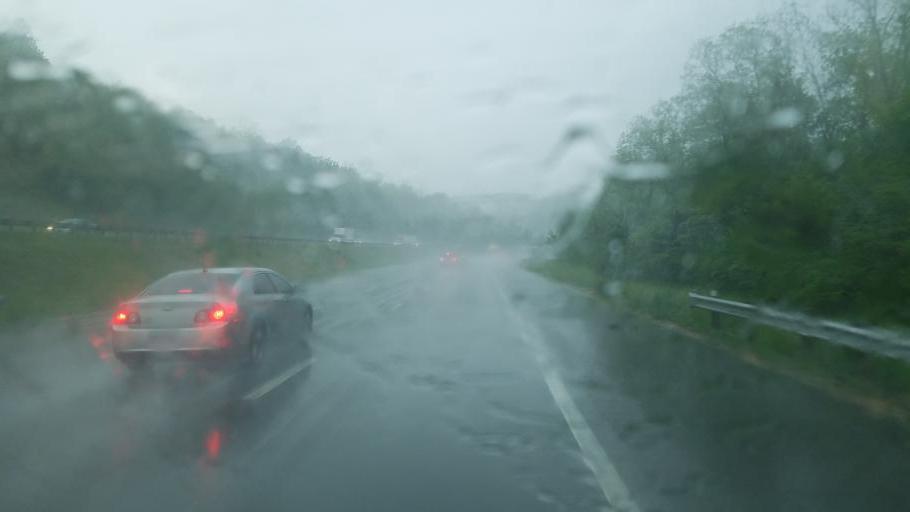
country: US
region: Ohio
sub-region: Hamilton County
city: Miamitown
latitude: 39.2184
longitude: -84.6694
